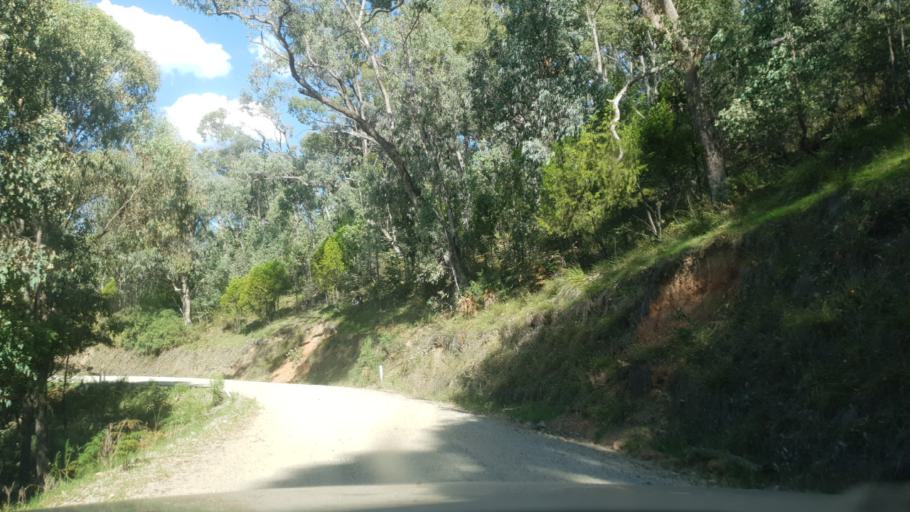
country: AU
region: Victoria
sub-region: Alpine
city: Mount Beauty
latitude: -36.7478
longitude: 147.1815
